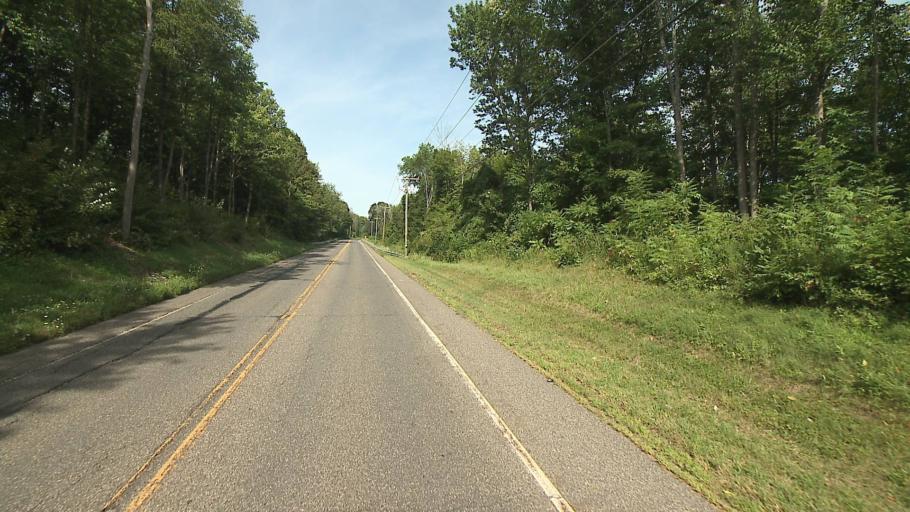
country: US
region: Connecticut
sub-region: Litchfield County
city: Thomaston
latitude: 41.7013
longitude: -73.1144
